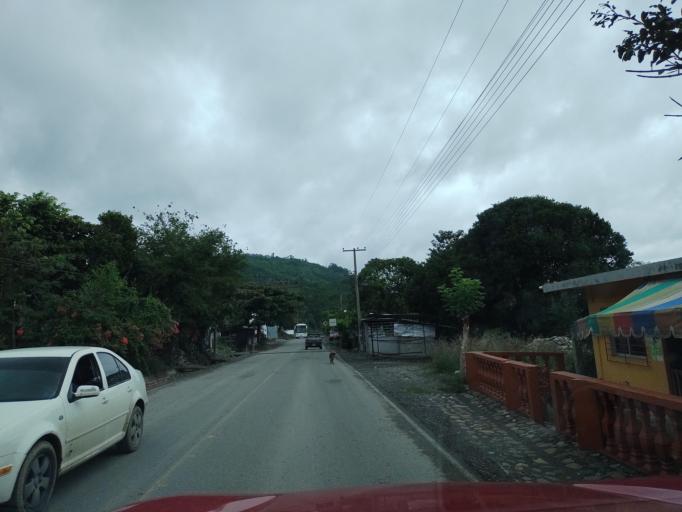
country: MX
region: Puebla
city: Espinal
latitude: 20.2615
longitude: -97.3725
